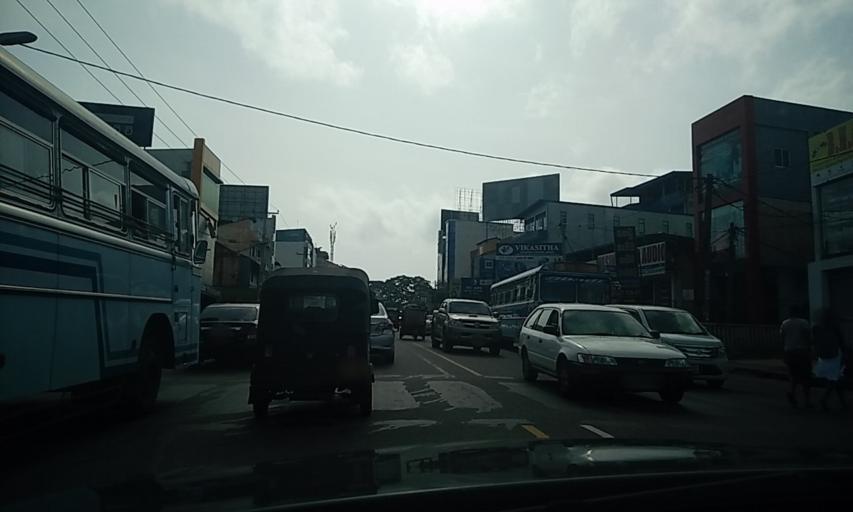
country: LK
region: Western
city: Sri Jayewardenepura Kotte
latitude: 6.8631
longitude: 79.9009
